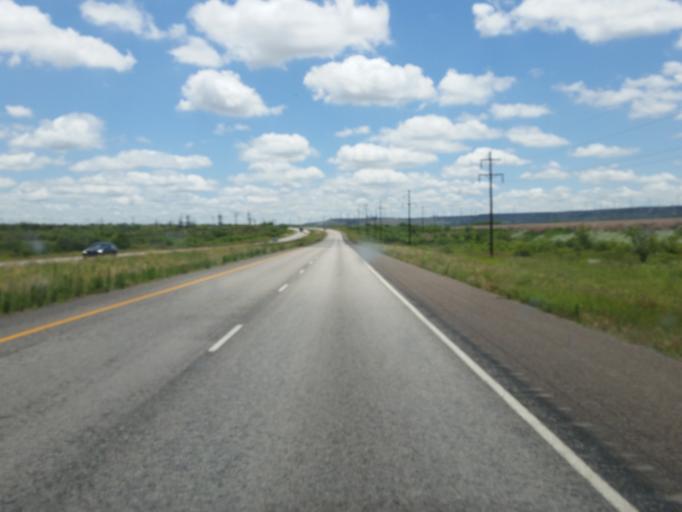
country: US
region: Texas
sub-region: Garza County
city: Post
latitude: 33.0061
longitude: -101.1669
